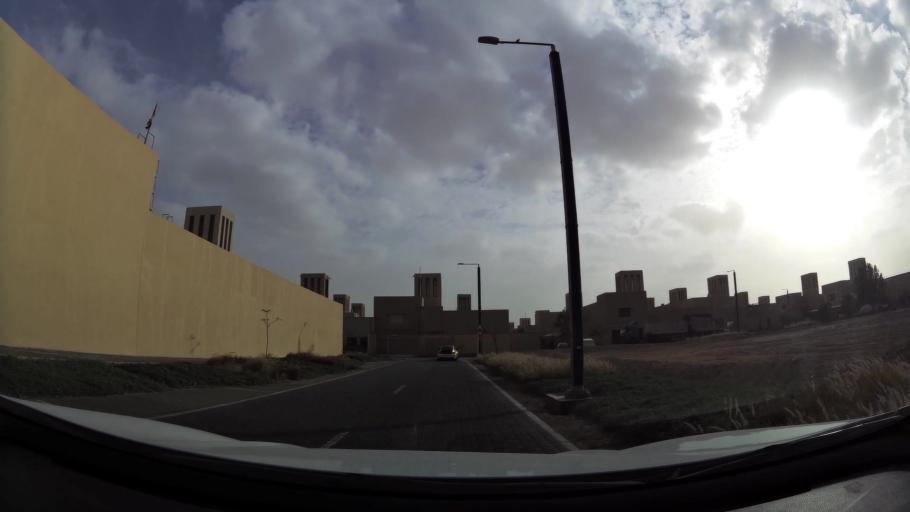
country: AE
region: Abu Dhabi
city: Abu Dhabi
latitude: 24.5030
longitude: 54.5955
